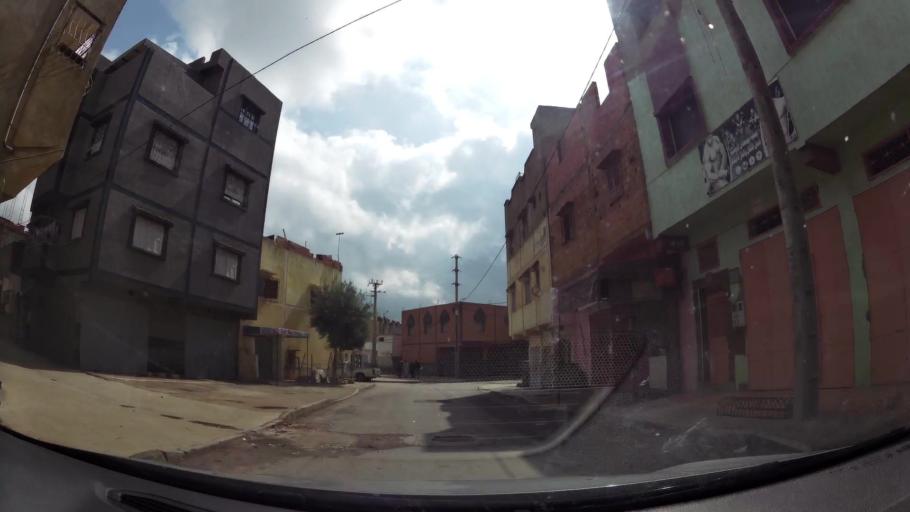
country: MA
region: Rabat-Sale-Zemmour-Zaer
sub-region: Khemisset
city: Tiflet
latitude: 33.8958
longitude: -6.3197
